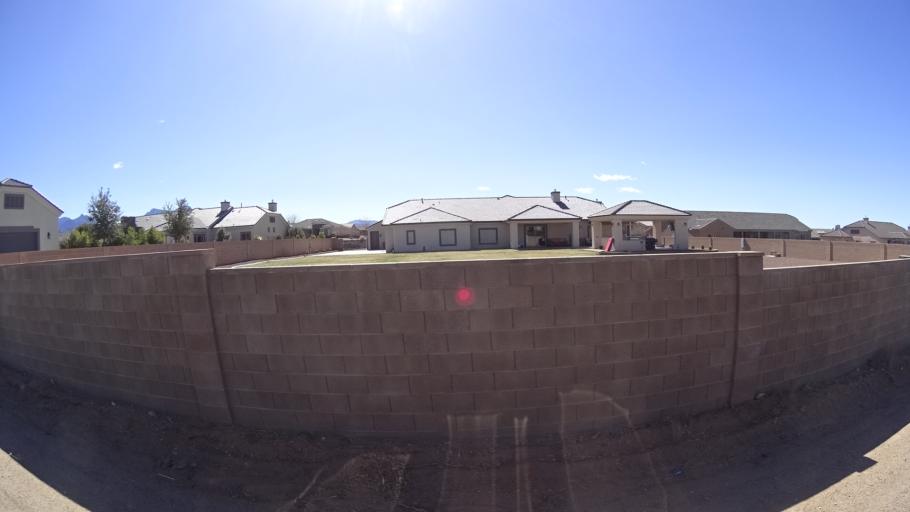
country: US
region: Arizona
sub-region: Mohave County
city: Kingman
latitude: 35.1958
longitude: -113.9991
